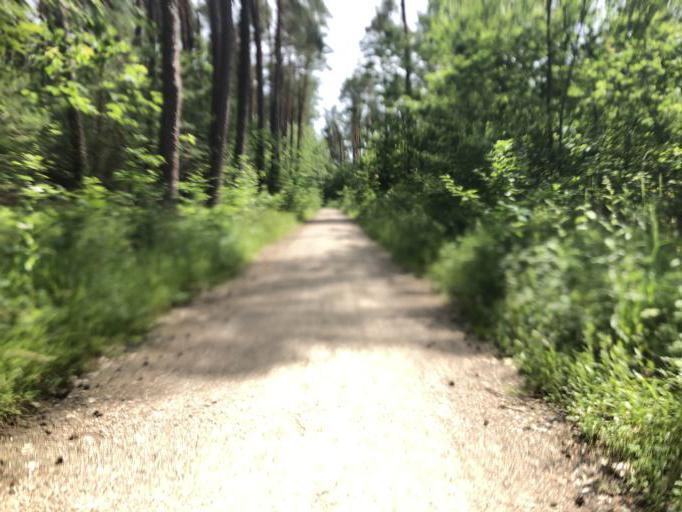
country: DE
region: Bavaria
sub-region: Regierungsbezirk Mittelfranken
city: Mohrendorf
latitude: 49.6153
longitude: 10.9604
